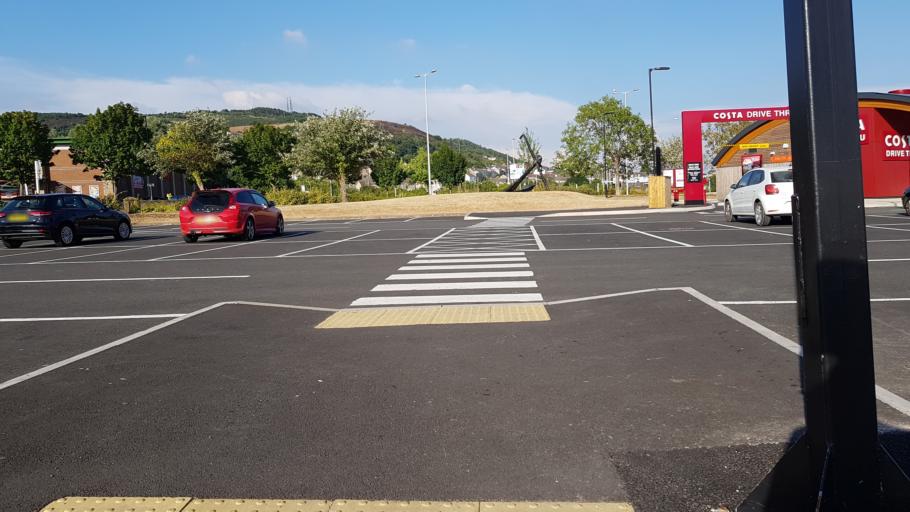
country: GB
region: Wales
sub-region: City and County of Swansea
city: Swansea
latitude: 51.6226
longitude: -3.9383
